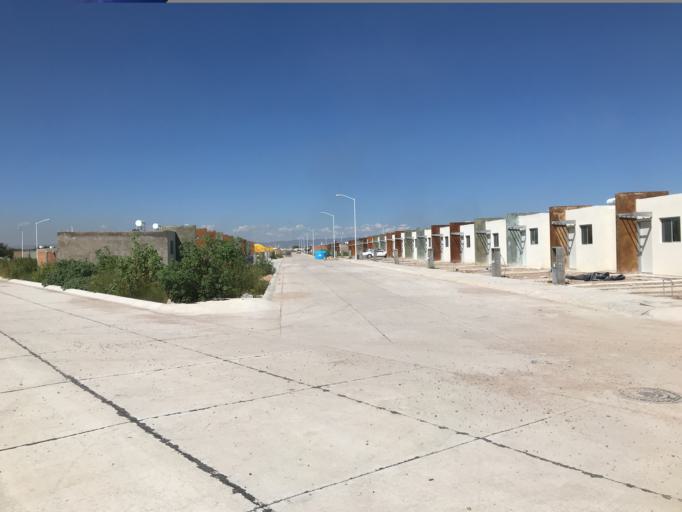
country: MX
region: Durango
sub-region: Durango
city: Sebastian Lerdo de Tejada
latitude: 24.0012
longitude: -104.5989
